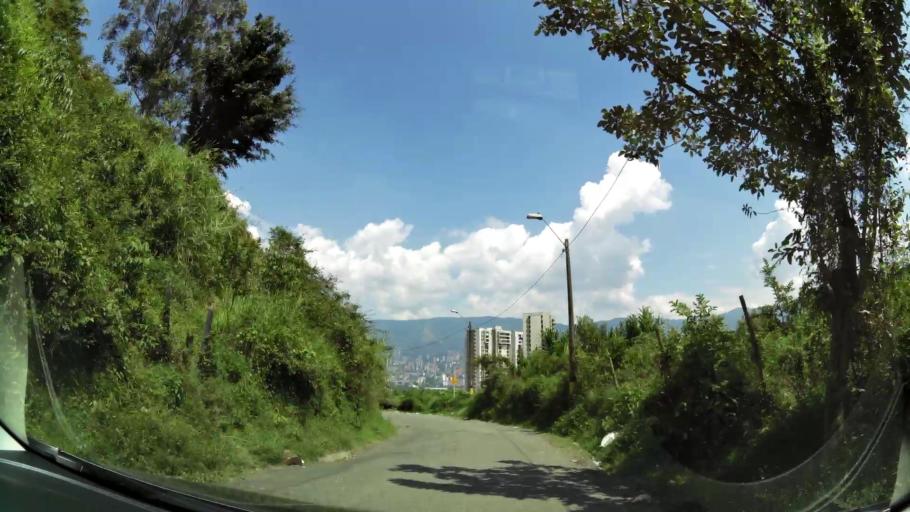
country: CO
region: Antioquia
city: Itagui
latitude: 6.2134
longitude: -75.6088
